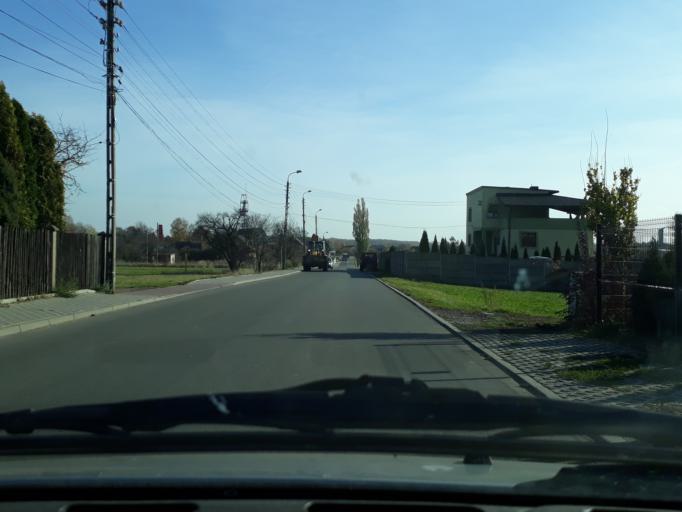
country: PL
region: Silesian Voivodeship
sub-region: Powiat tarnogorski
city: Tarnowskie Gory
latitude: 50.4274
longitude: 18.8453
